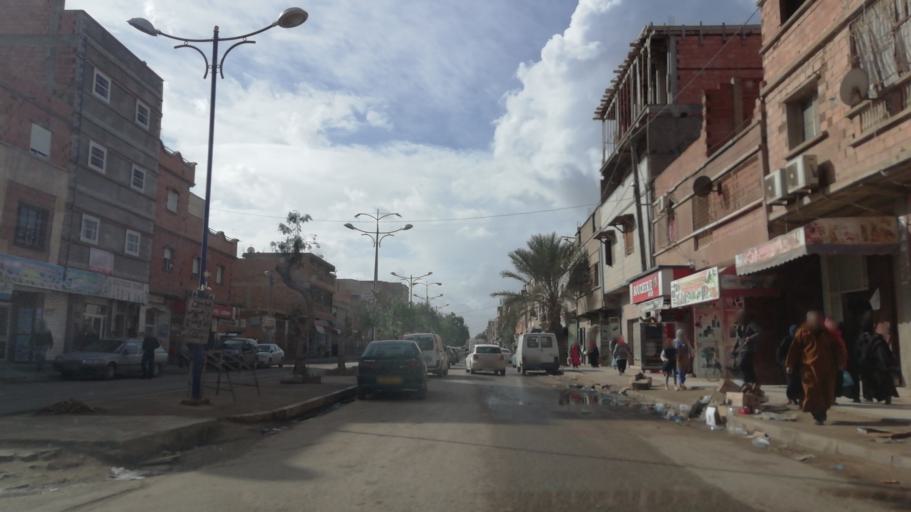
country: DZ
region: Oran
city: Es Senia
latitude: 35.6449
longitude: -0.5720
